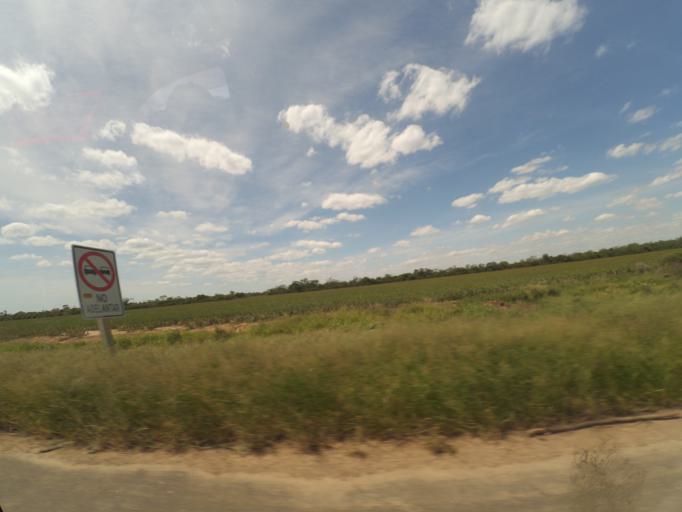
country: BO
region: Santa Cruz
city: Pailon
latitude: -17.5897
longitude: -61.9728
